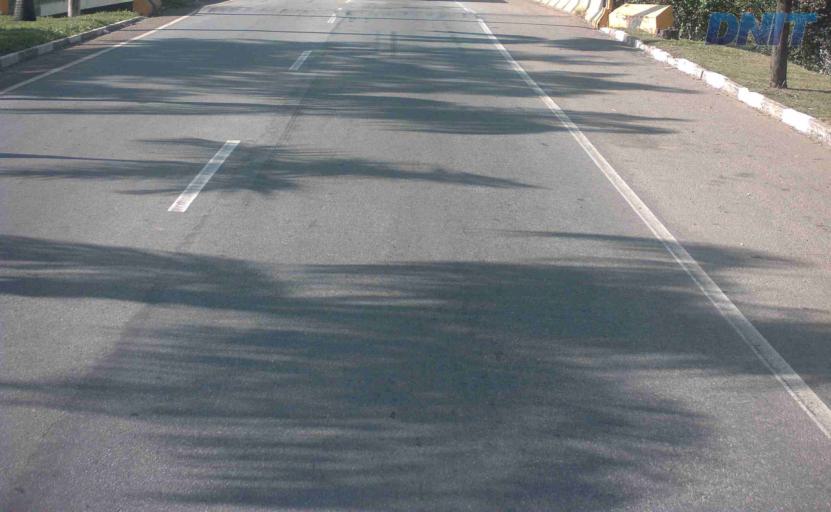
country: BR
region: Minas Gerais
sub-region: Ipatinga
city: Ipatinga
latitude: -19.4646
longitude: -42.5345
